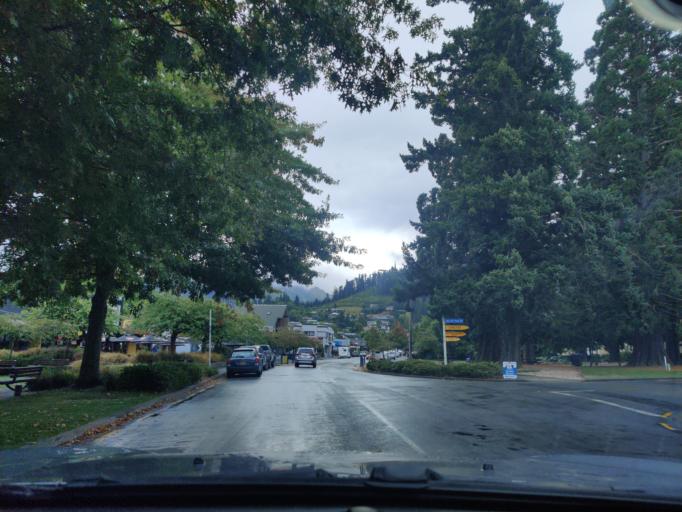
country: NZ
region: Canterbury
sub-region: Hurunui District
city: Amberley
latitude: -42.5220
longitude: 172.8298
